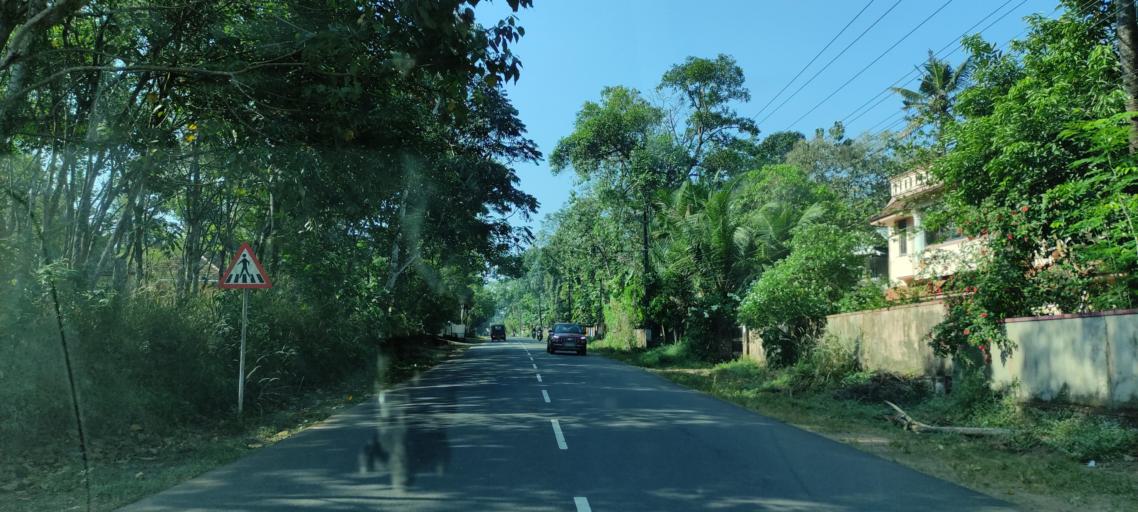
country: IN
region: Kerala
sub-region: Pattanamtitta
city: Adur
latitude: 9.1162
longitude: 76.6992
